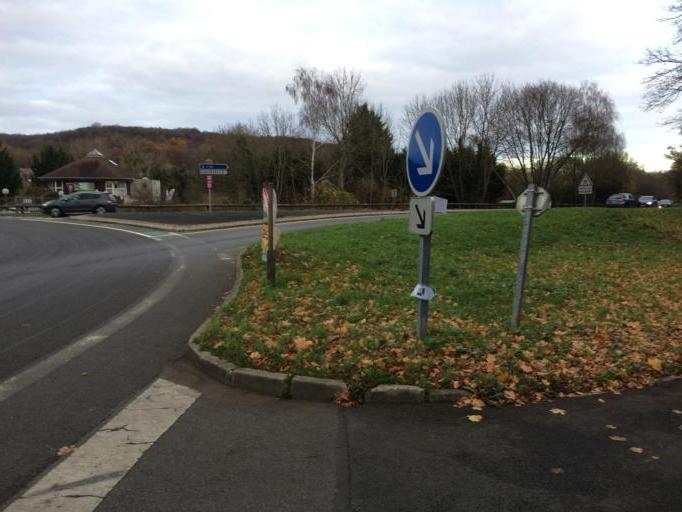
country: FR
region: Ile-de-France
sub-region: Departement de l'Essonne
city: Igny
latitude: 48.7357
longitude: 2.2383
